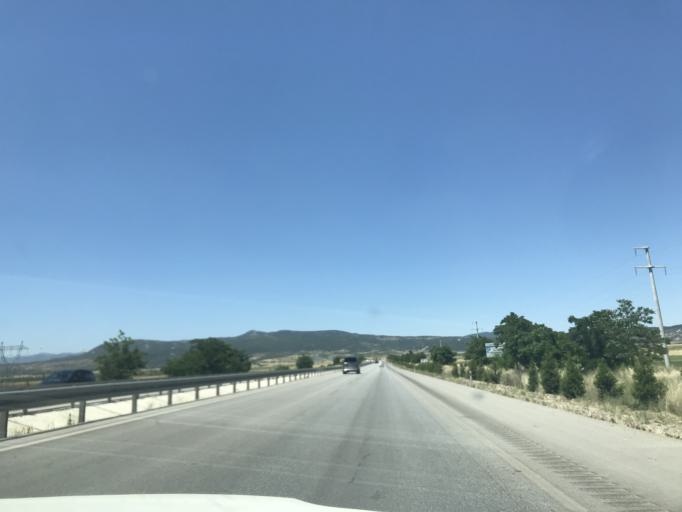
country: TR
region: Isparta
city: Keciborlu
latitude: 37.8982
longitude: 30.3690
